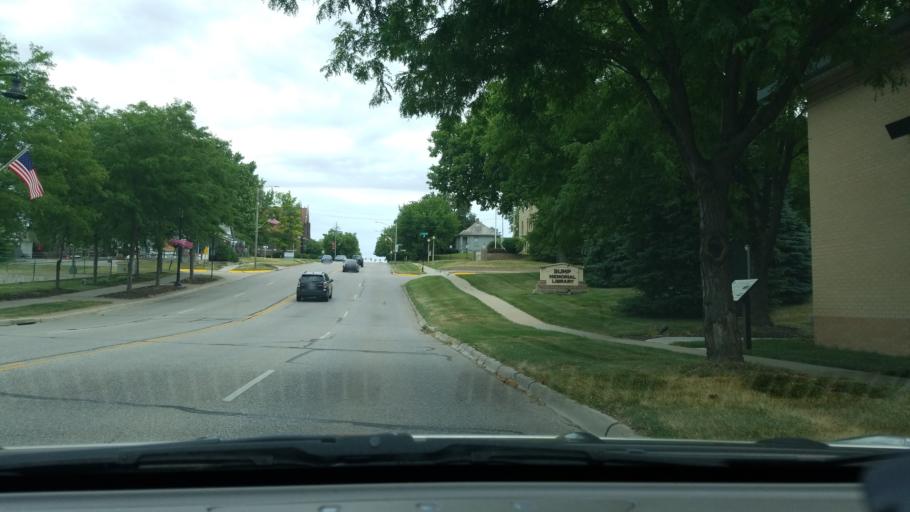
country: US
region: Nebraska
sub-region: Sarpy County
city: Papillion
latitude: 41.1578
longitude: -96.0429
